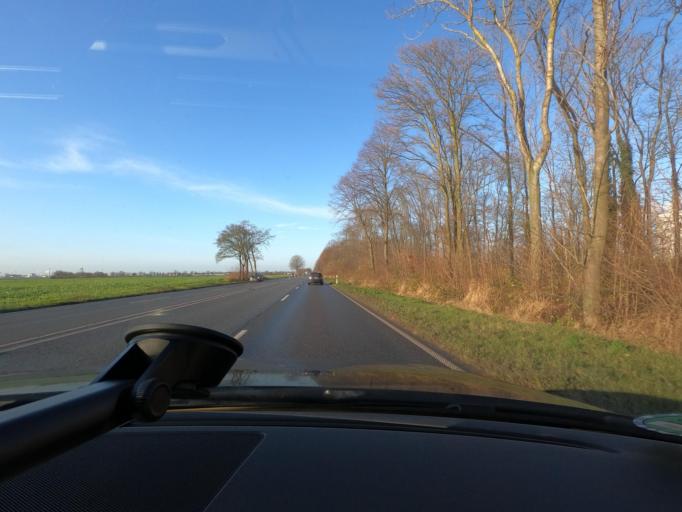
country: DE
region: North Rhine-Westphalia
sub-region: Regierungsbezirk Dusseldorf
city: Hochfeld
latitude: 51.3547
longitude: 6.7152
